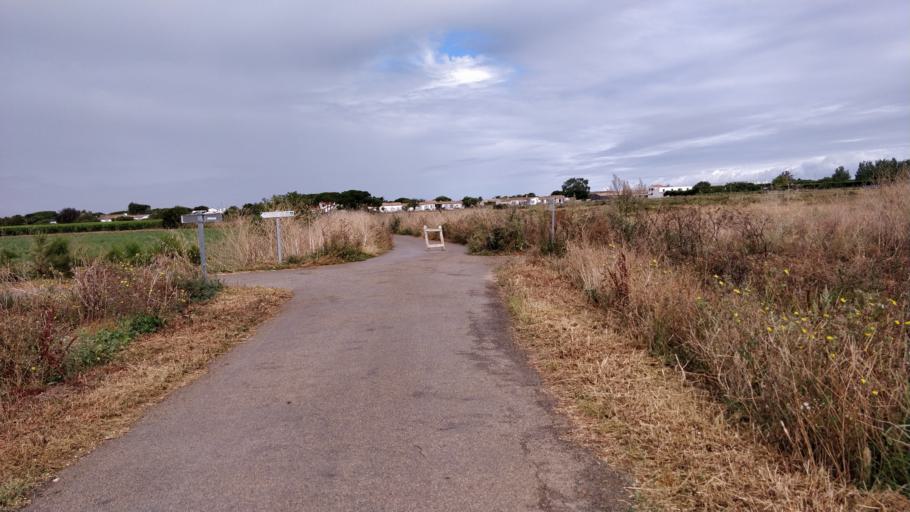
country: FR
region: Poitou-Charentes
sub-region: Departement de la Charente-Maritime
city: La Couarde-sur-Mer
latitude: 46.2238
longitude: -1.4251
